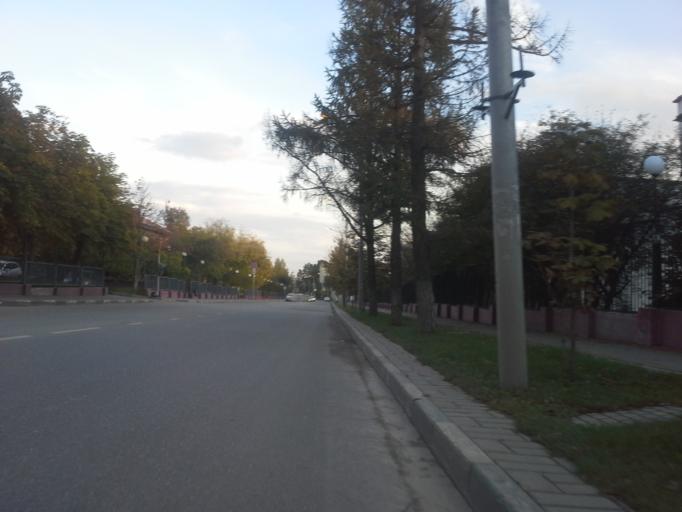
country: RU
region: Moskovskaya
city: Kommunarka
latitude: 55.5816
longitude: 37.4762
